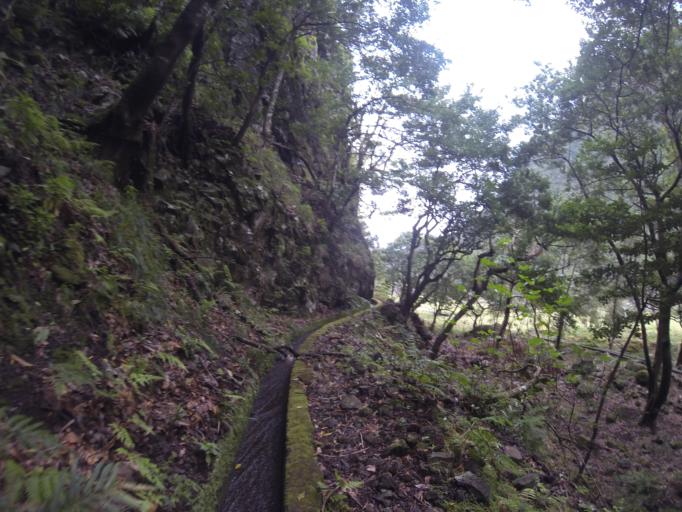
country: PT
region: Madeira
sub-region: Sao Vicente
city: Sao Vicente
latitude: 32.7933
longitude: -17.1133
